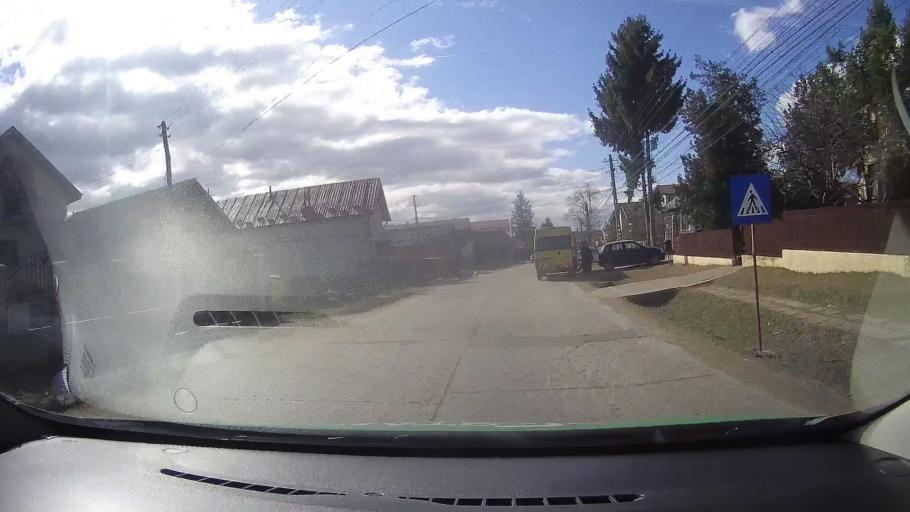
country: RO
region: Dambovita
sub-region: Comuna Branesti
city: Branesti
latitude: 45.0376
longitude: 25.4171
